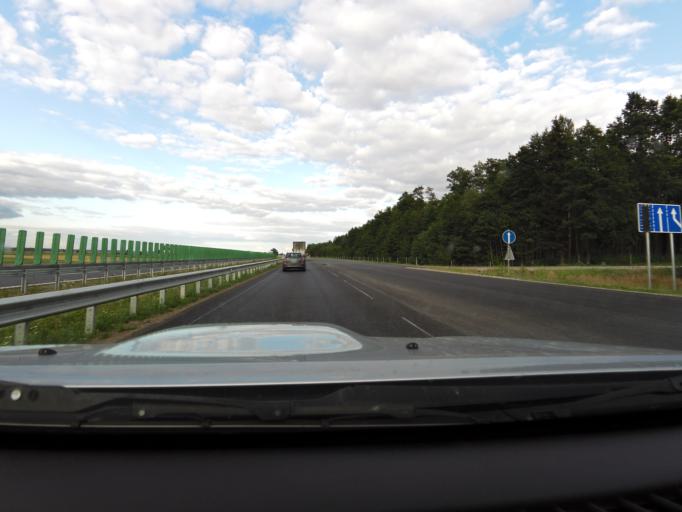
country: LT
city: Kazlu Ruda
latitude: 54.6757
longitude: 23.5649
